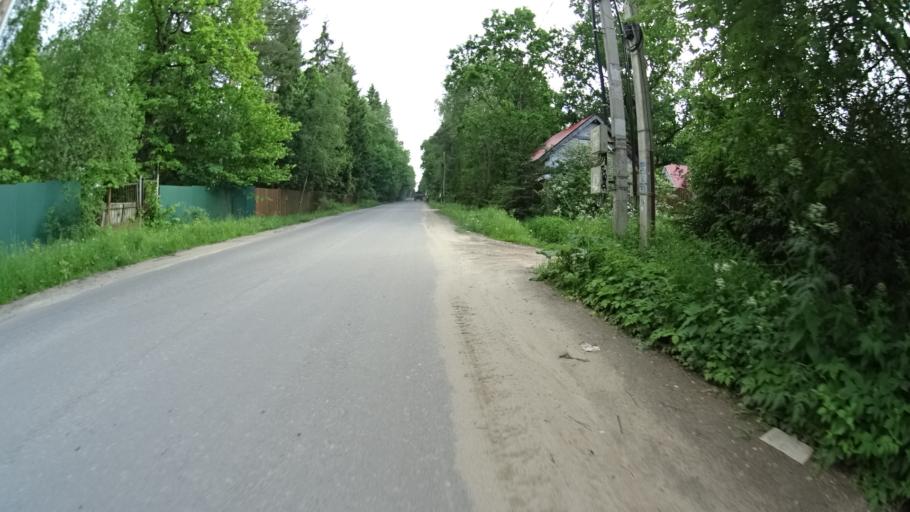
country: RU
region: Moskovskaya
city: Zelenogradskiy
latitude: 56.1205
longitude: 37.9282
